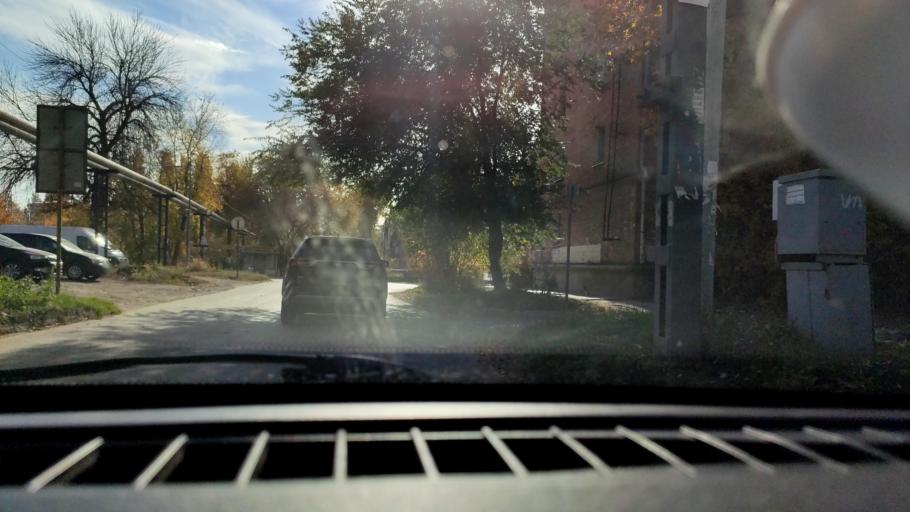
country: RU
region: Samara
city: Petra-Dubrava
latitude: 53.2962
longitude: 50.2900
